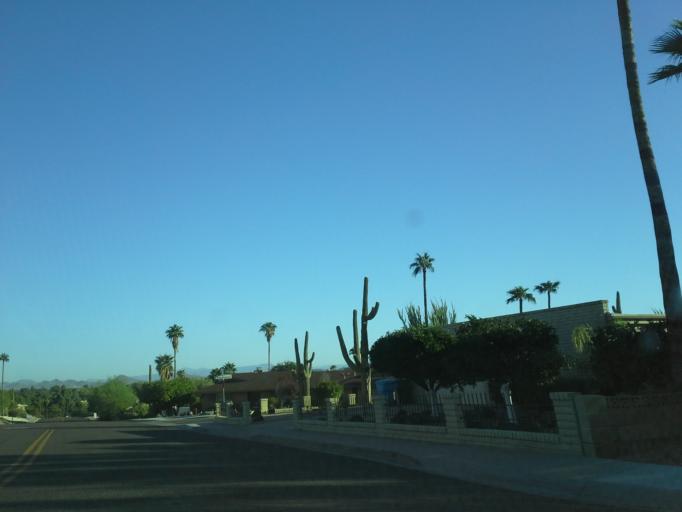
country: US
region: Arizona
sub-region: Maricopa County
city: Glendale
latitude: 33.6038
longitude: -112.0840
